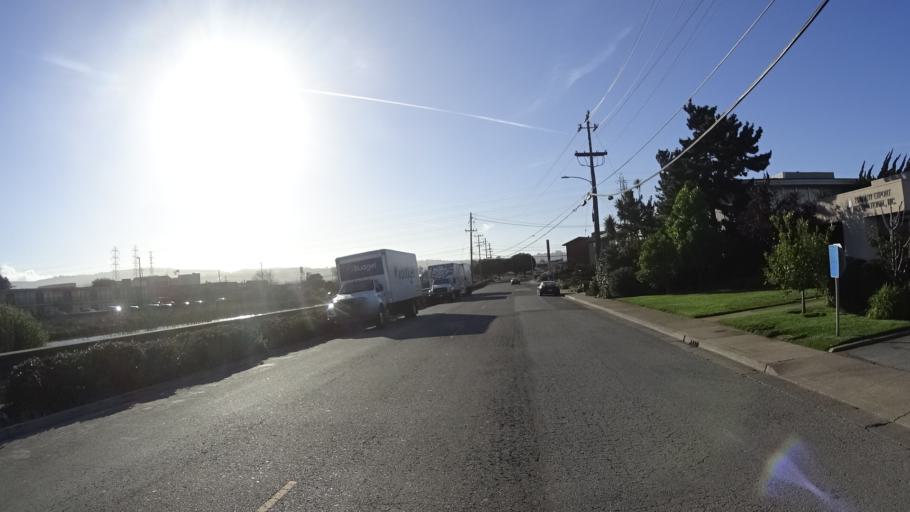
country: US
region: California
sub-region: San Mateo County
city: South San Francisco
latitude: 37.6493
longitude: -122.4027
